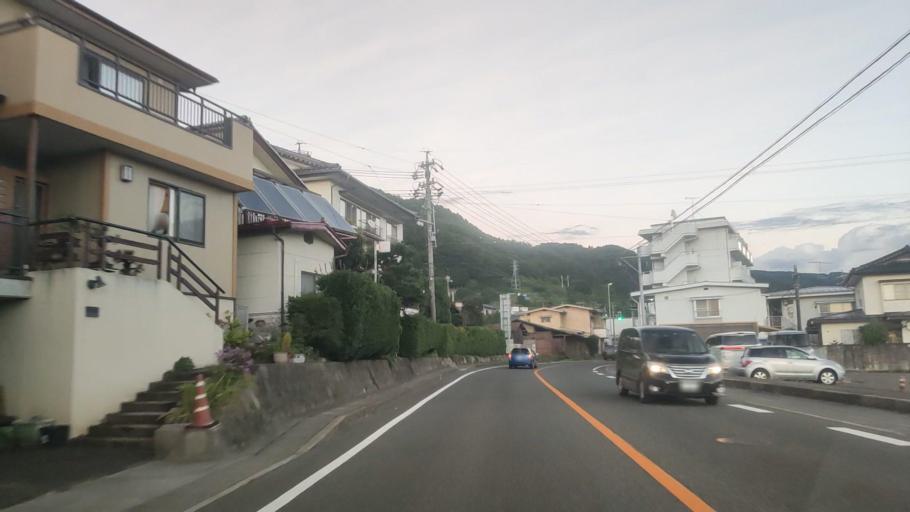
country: JP
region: Nagano
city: Suwa
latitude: 36.0711
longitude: 138.0926
